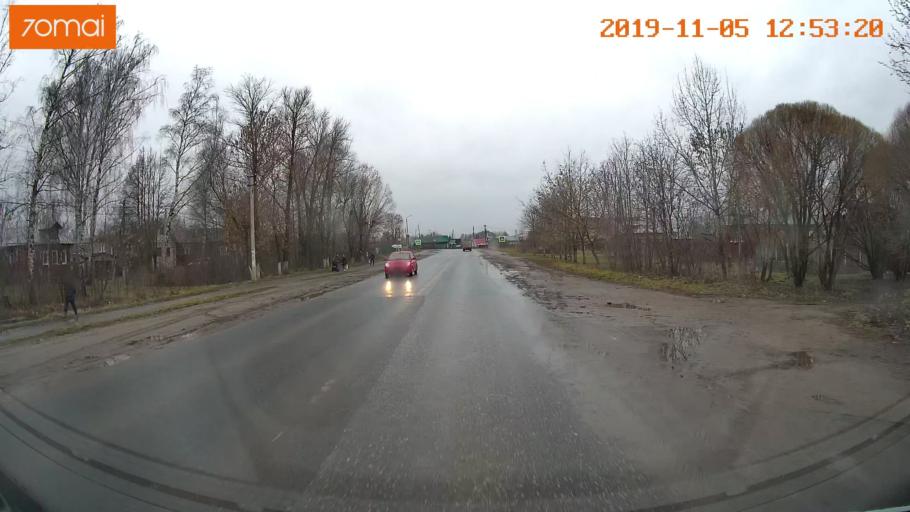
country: RU
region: Ivanovo
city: Kokhma
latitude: 56.9366
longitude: 41.0989
